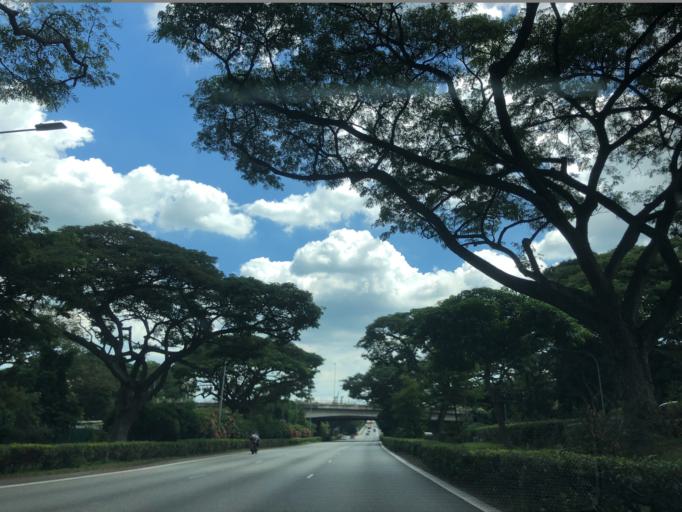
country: SG
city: Singapore
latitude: 1.2763
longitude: 103.8278
